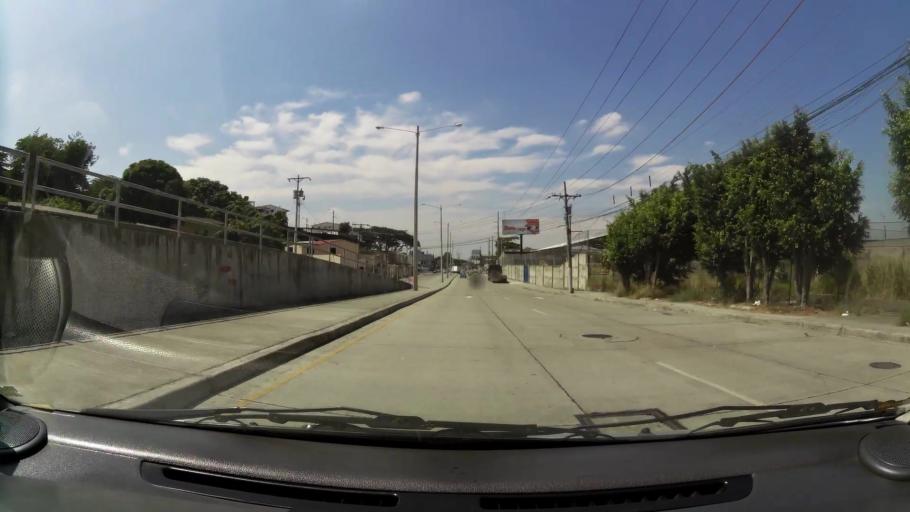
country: EC
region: Guayas
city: Guayaquil
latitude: -2.1366
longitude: -79.9162
